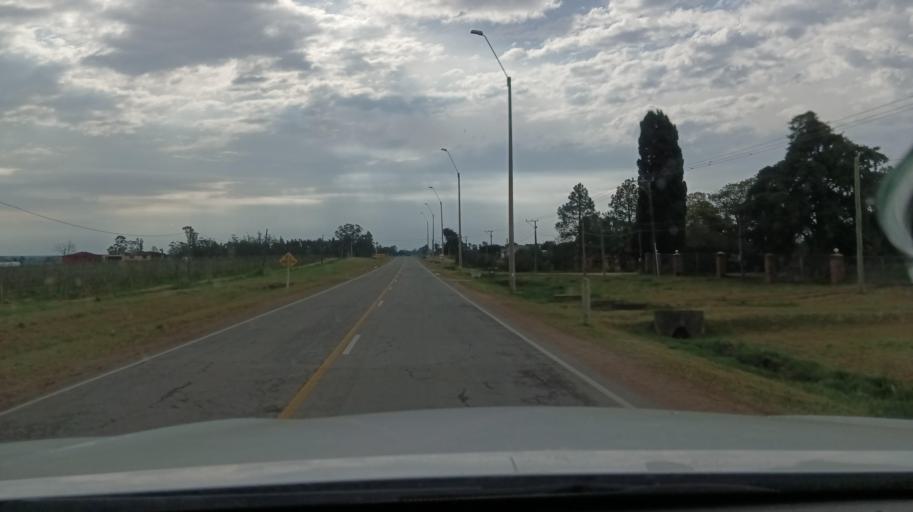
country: UY
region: Canelones
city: Toledo
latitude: -34.7018
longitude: -56.1050
